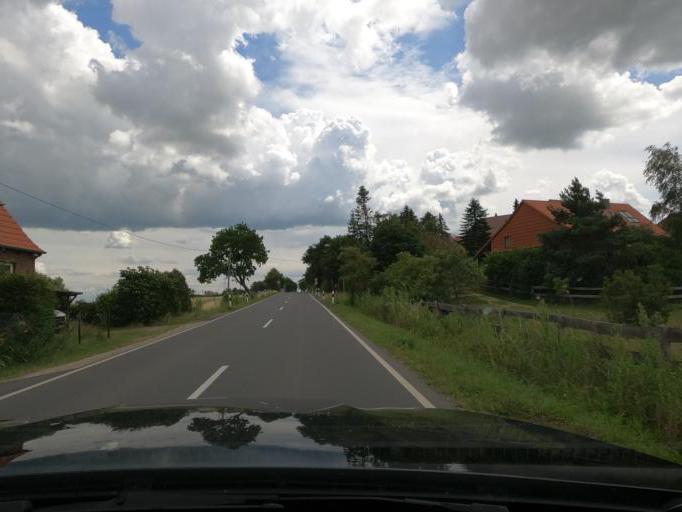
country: DE
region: Lower Saxony
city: Sehnde
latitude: 52.2984
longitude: 9.9873
